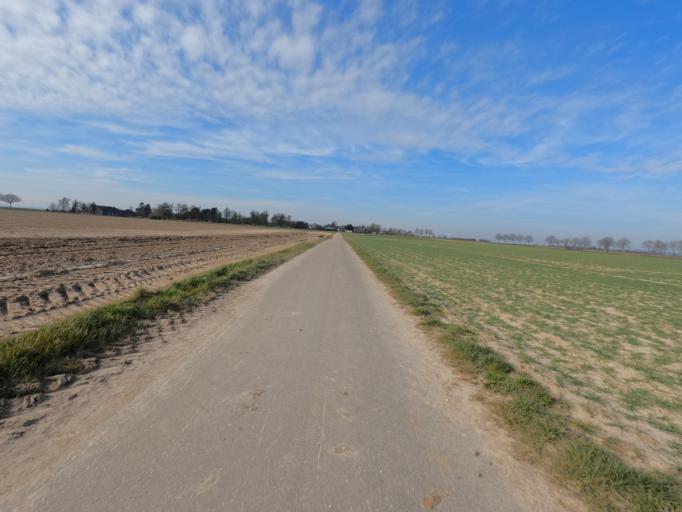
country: DE
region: North Rhine-Westphalia
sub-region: Regierungsbezirk Koln
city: Linnich
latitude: 50.9913
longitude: 6.3192
